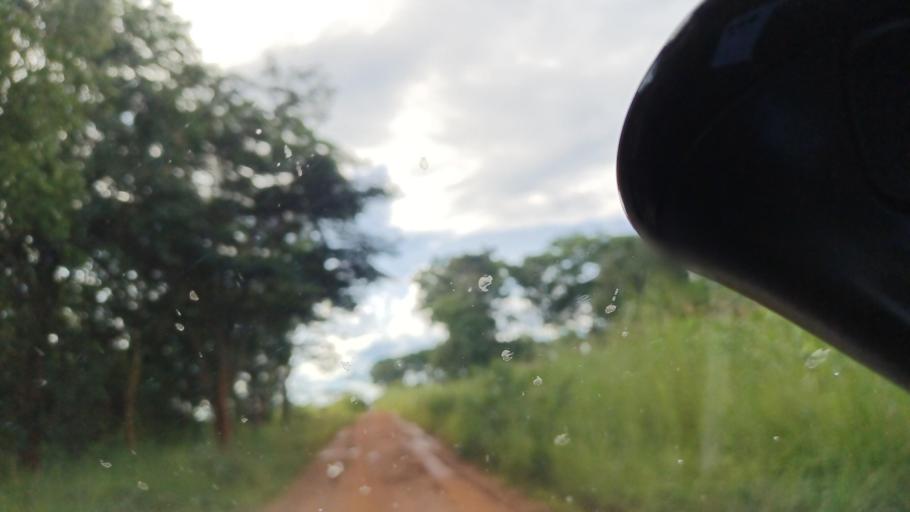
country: ZM
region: North-Western
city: Kasempa
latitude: -13.6807
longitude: 26.3140
